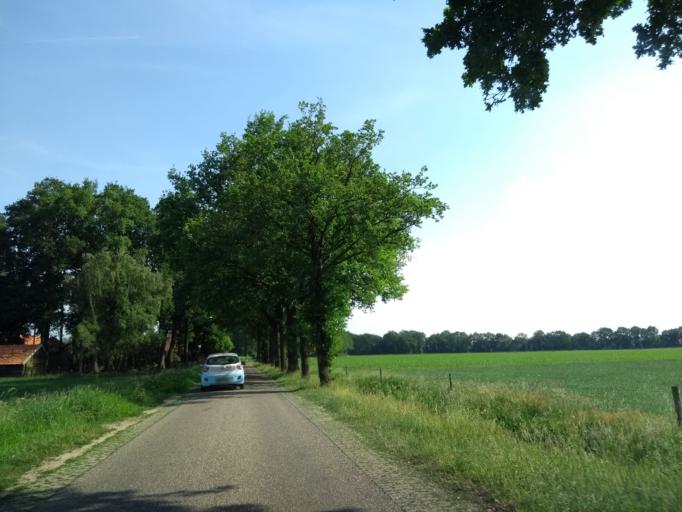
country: DE
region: Lower Saxony
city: Nordhorn
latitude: 52.3732
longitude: 7.0326
